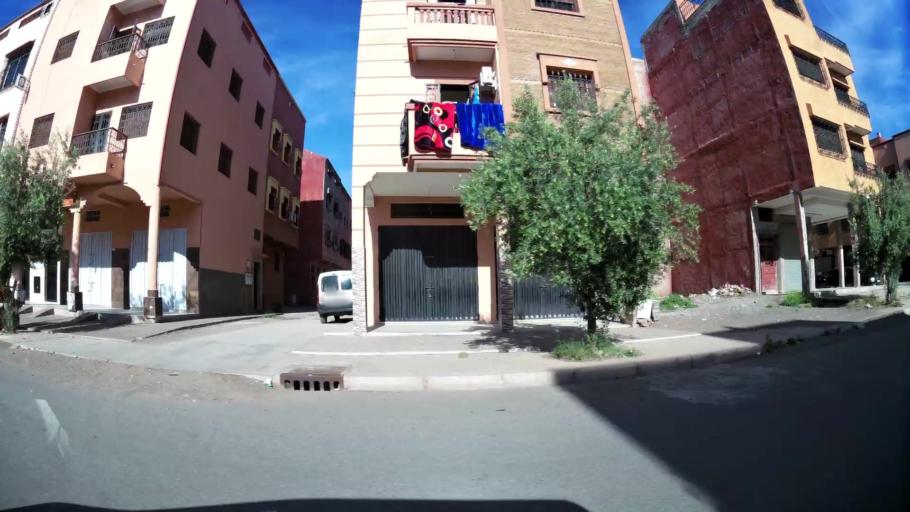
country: MA
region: Marrakech-Tensift-Al Haouz
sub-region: Marrakech
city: Marrakesh
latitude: 31.6856
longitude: -8.0743
